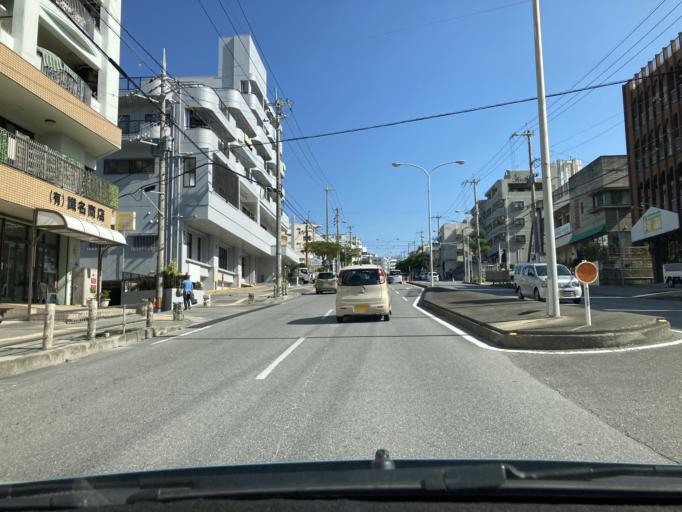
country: JP
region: Okinawa
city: Naha-shi
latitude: 26.2056
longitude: 127.7021
